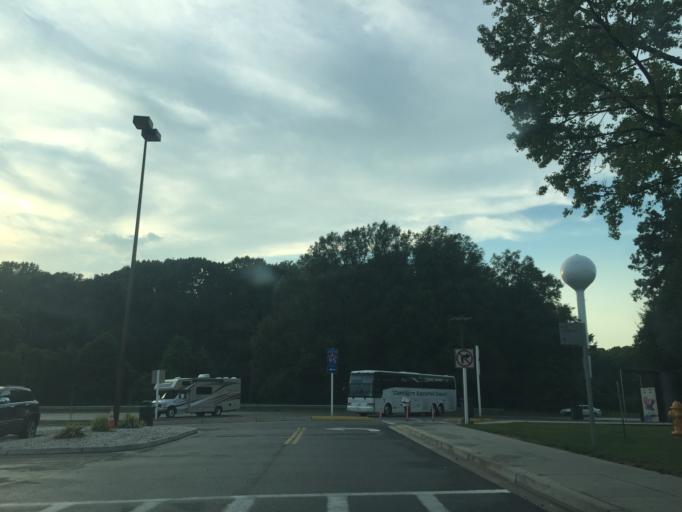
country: US
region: Maryland
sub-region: Harford County
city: Riverside
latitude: 39.4972
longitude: -76.2327
